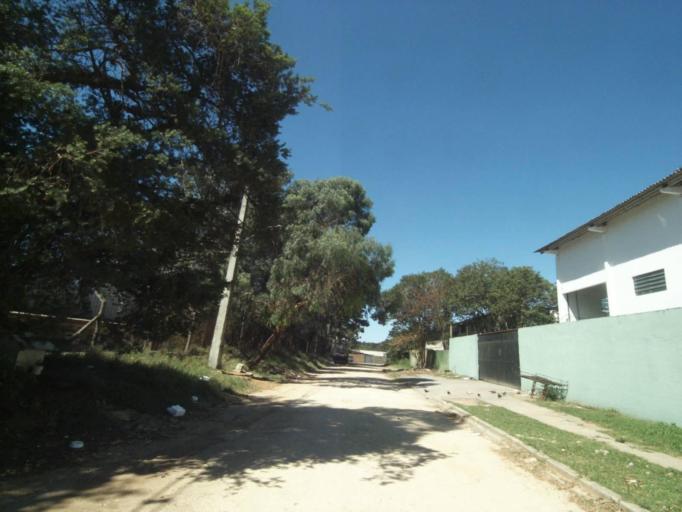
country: BR
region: Parana
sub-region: Curitiba
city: Curitiba
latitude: -25.4698
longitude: -49.3525
